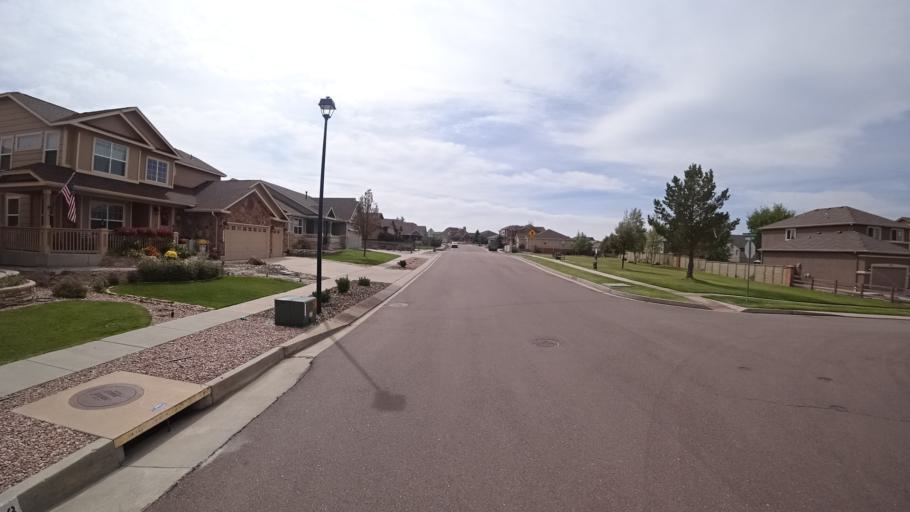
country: US
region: Colorado
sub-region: El Paso County
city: Cimarron Hills
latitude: 38.9217
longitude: -104.6895
